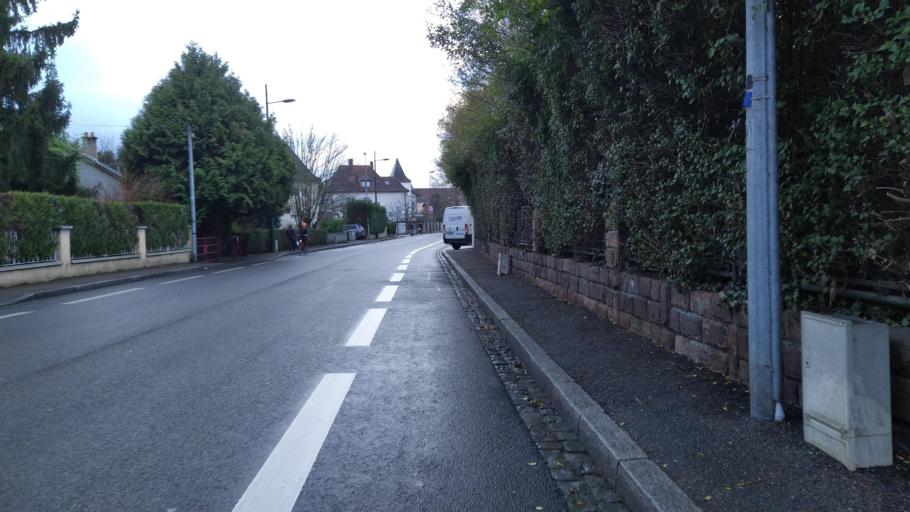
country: FR
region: Alsace
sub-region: Departement du Bas-Rhin
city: Schiltigheim
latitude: 48.6017
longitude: 7.7489
